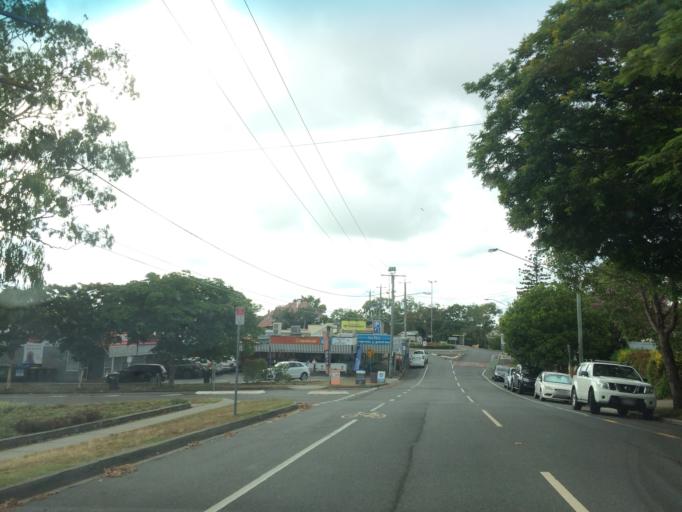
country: AU
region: Queensland
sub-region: Brisbane
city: Toowong
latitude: -27.5011
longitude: 152.9960
